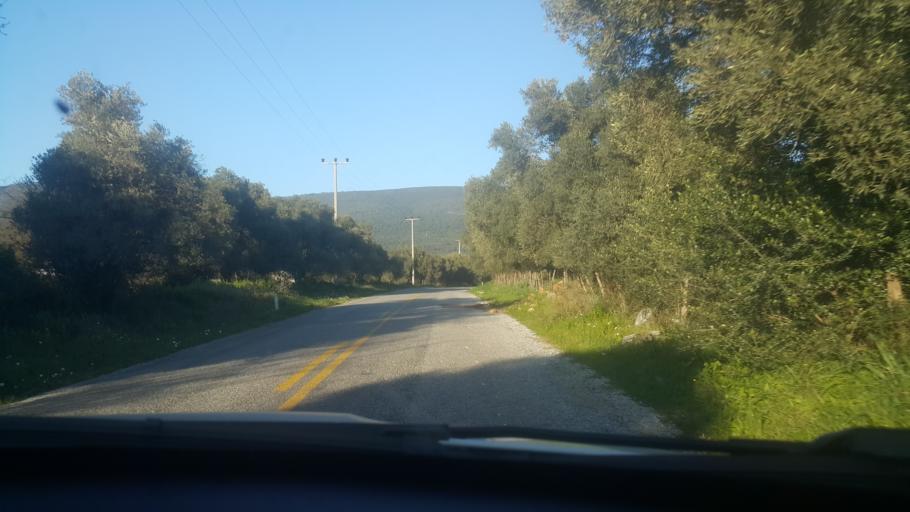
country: TR
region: Mugla
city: Kiulukioi
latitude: 37.2965
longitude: 27.5982
